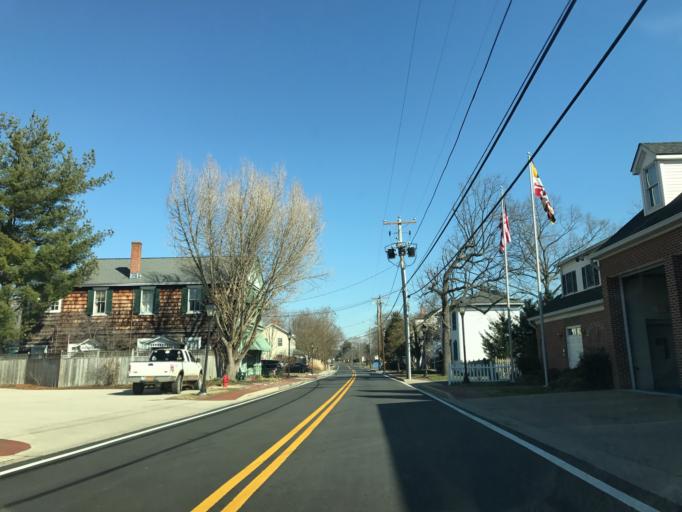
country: US
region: Maryland
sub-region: Queen Anne's County
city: Grasonville
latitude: 38.9907
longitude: -76.1570
